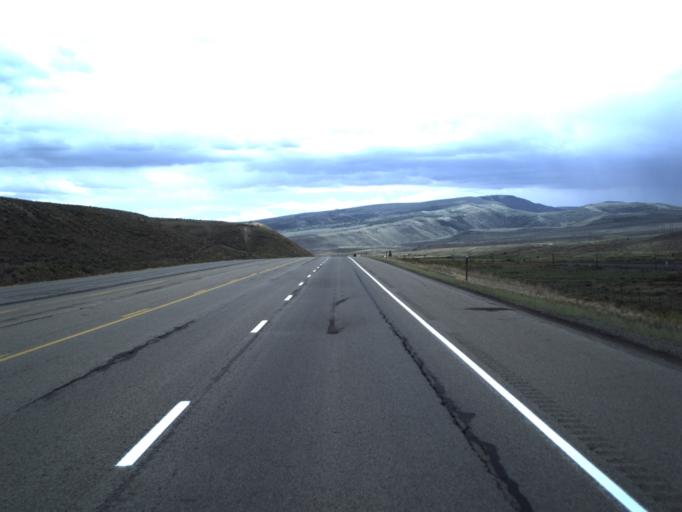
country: US
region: Utah
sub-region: Carbon County
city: Helper
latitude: 39.8728
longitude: -111.0341
